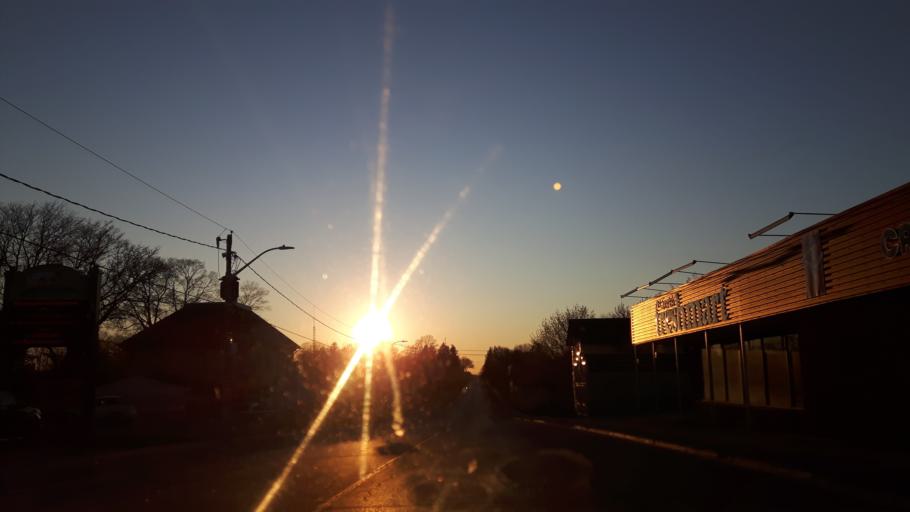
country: CA
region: Ontario
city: Bluewater
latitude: 43.6172
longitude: -81.5401
